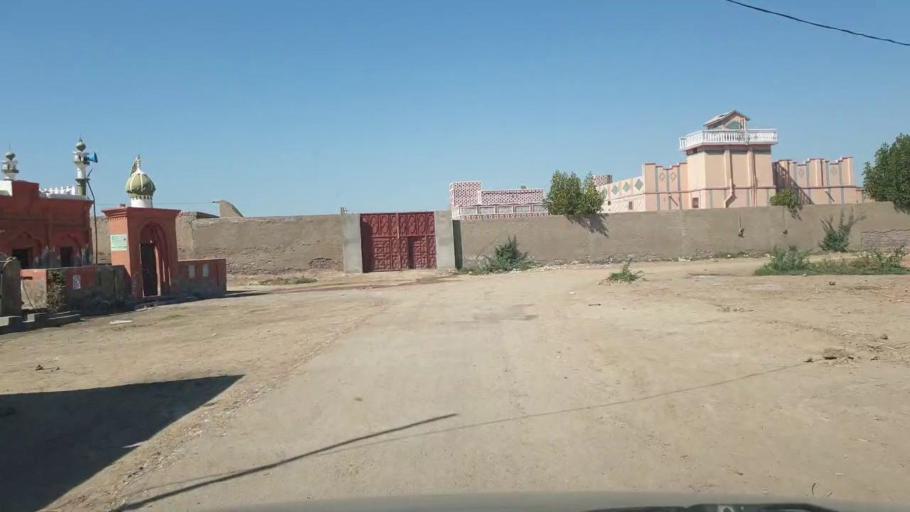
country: PK
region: Sindh
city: Dhoro Naro
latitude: 25.4037
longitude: 69.6178
